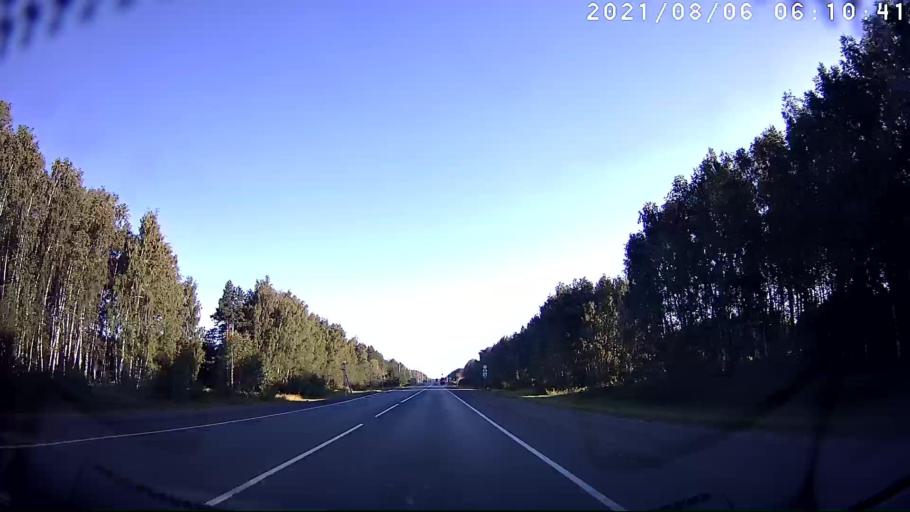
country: RU
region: Mariy-El
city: Pomary
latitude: 55.9385
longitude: 48.3715
